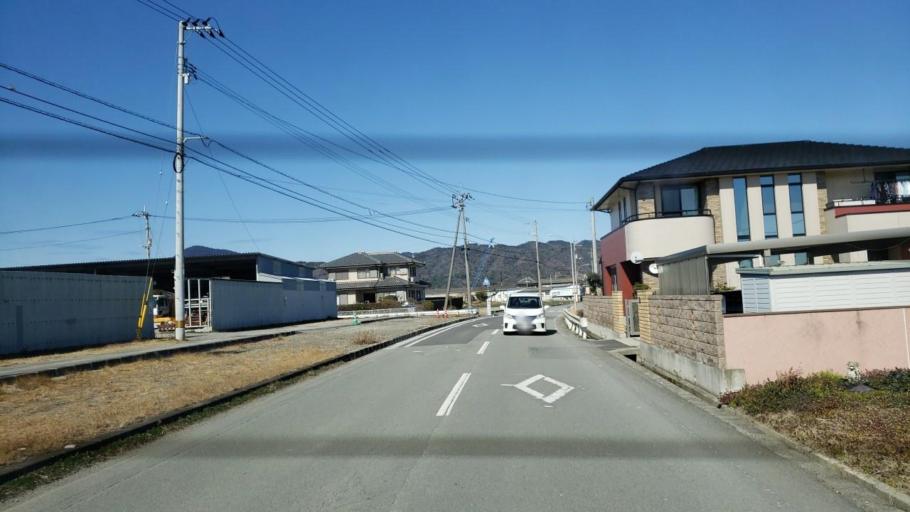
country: JP
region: Tokushima
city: Tokushima-shi
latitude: 34.1381
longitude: 134.5318
